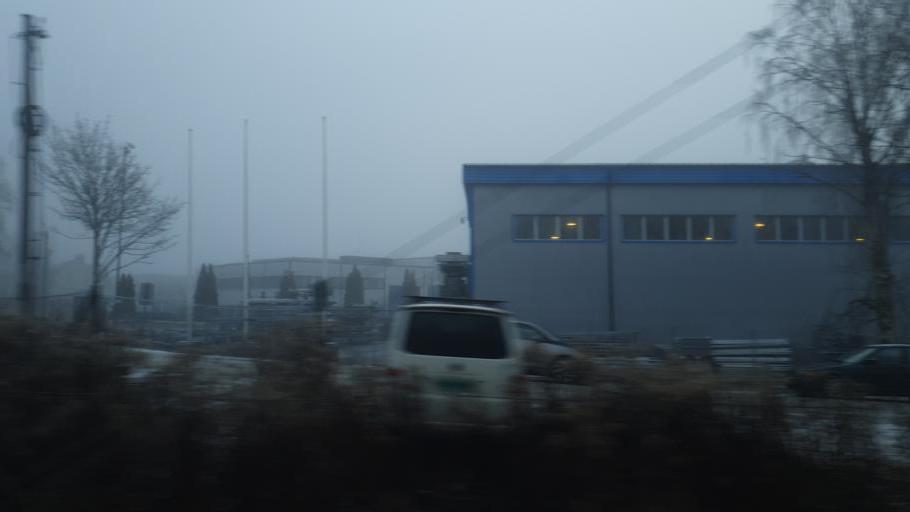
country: NO
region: Buskerud
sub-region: Lier
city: Lierbyen
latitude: 59.7526
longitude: 10.2650
